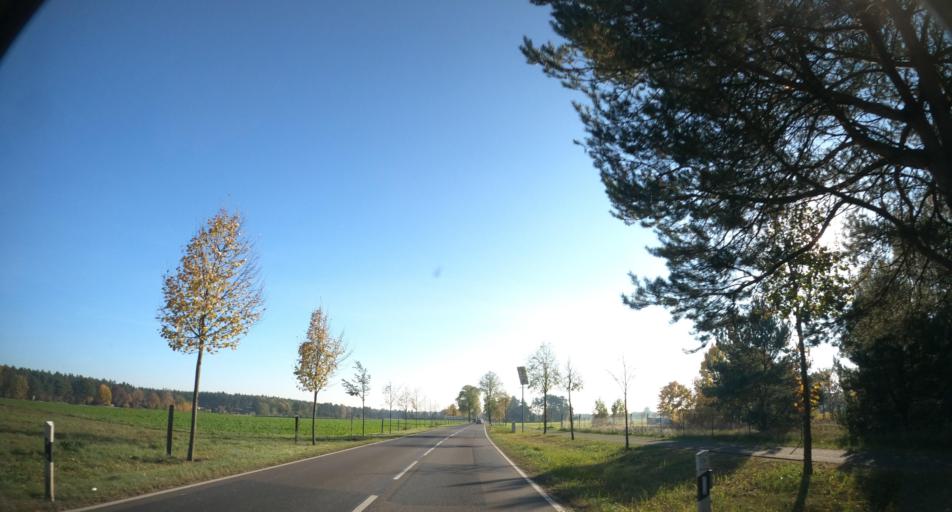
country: DE
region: Mecklenburg-Vorpommern
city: Ueckermunde
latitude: 53.7127
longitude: 14.0674
